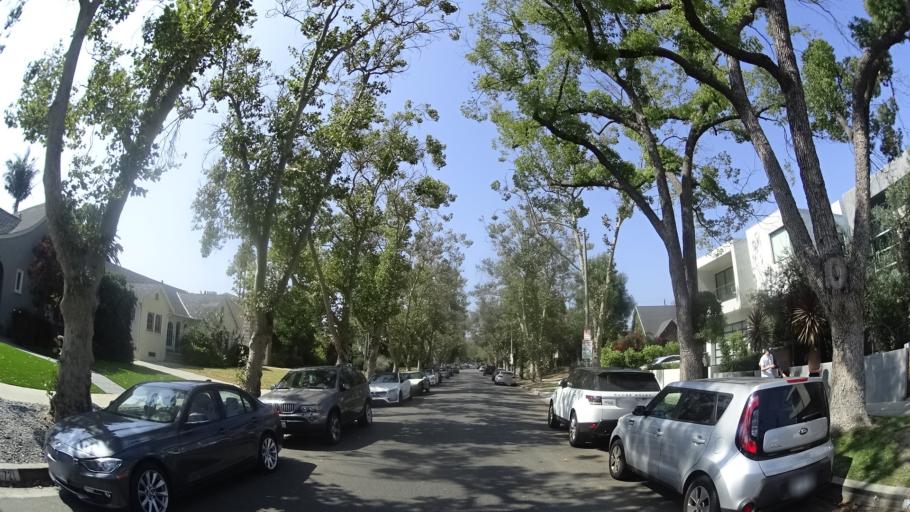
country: US
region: California
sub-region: Los Angeles County
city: West Hollywood
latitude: 34.0842
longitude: -118.3511
